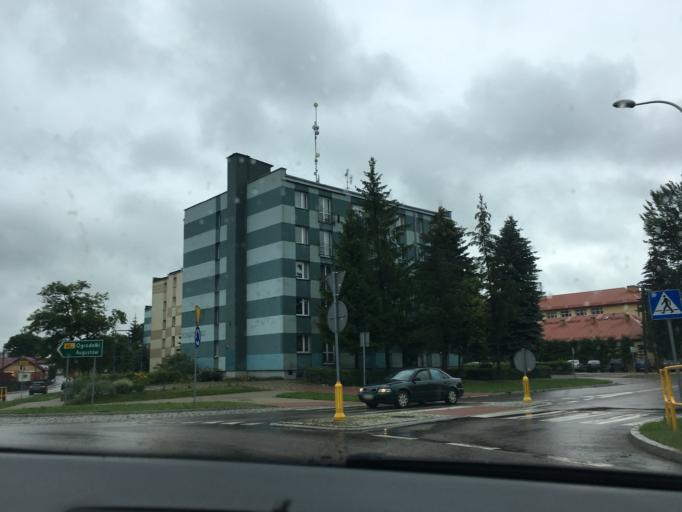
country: PL
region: Podlasie
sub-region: Powiat sejnenski
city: Sejny
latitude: 54.1080
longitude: 23.3405
